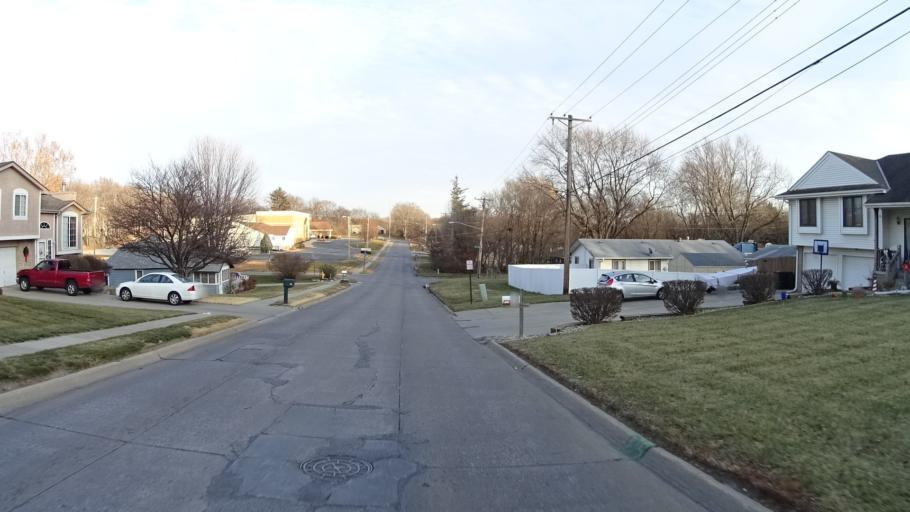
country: US
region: Nebraska
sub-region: Sarpy County
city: La Vista
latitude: 41.1764
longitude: -95.9707
